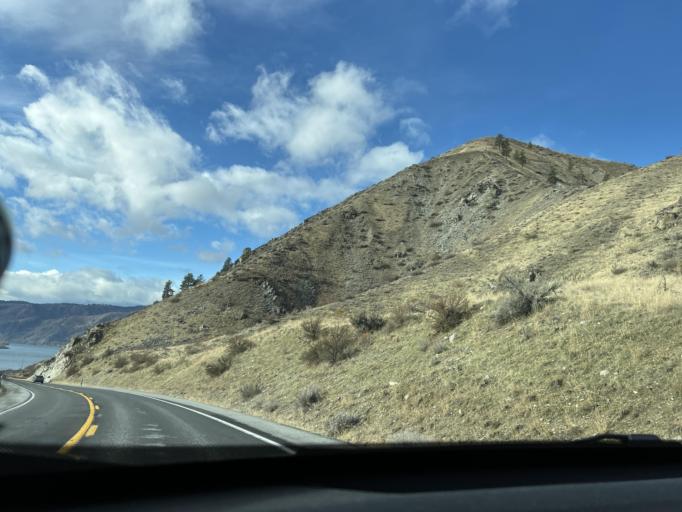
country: US
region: Washington
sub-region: Chelan County
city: Manson
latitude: 47.7752
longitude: -120.1560
